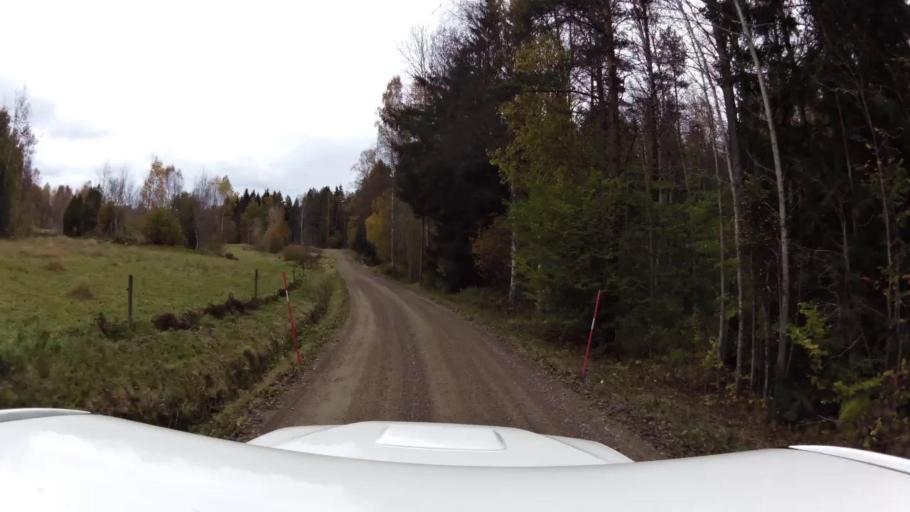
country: SE
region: OEstergoetland
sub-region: Linkopings Kommun
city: Ljungsbro
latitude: 58.5794
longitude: 15.4605
